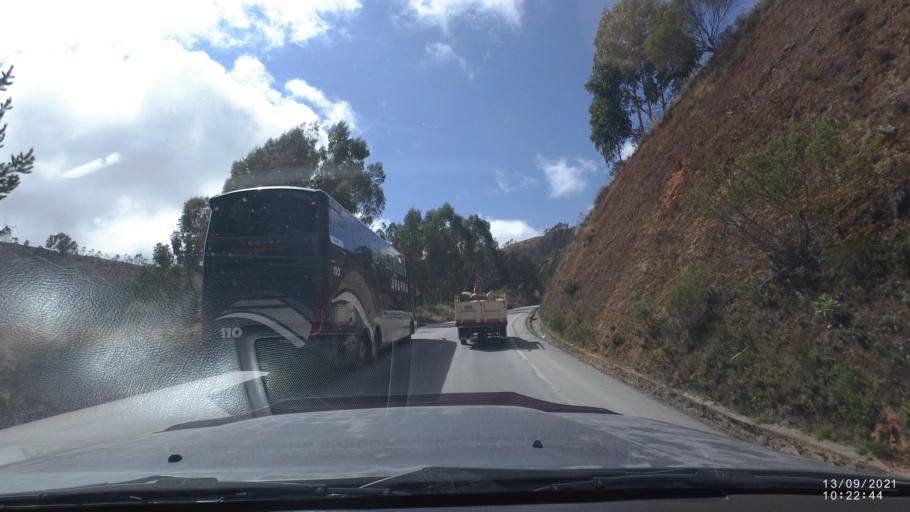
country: BO
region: Cochabamba
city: Colomi
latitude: -17.3165
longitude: -65.8713
